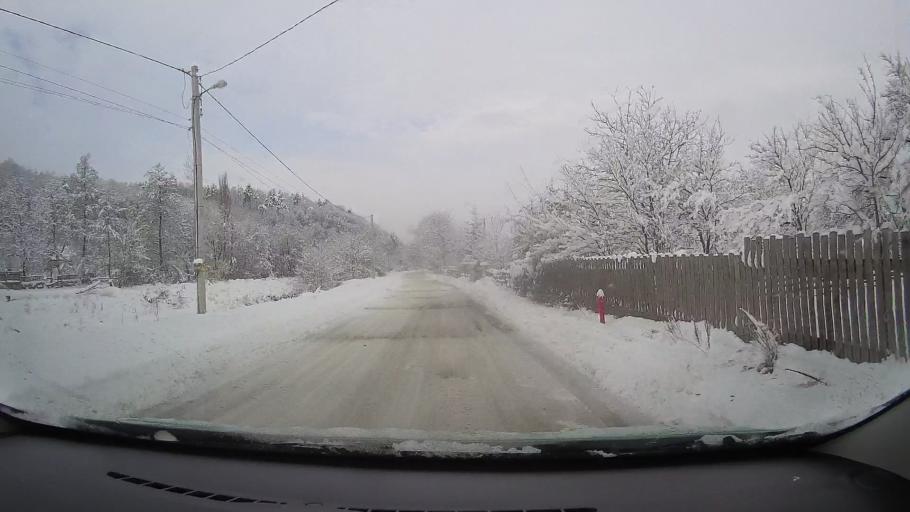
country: RO
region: Alba
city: Pianu de Sus
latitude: 45.8831
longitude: 23.4915
